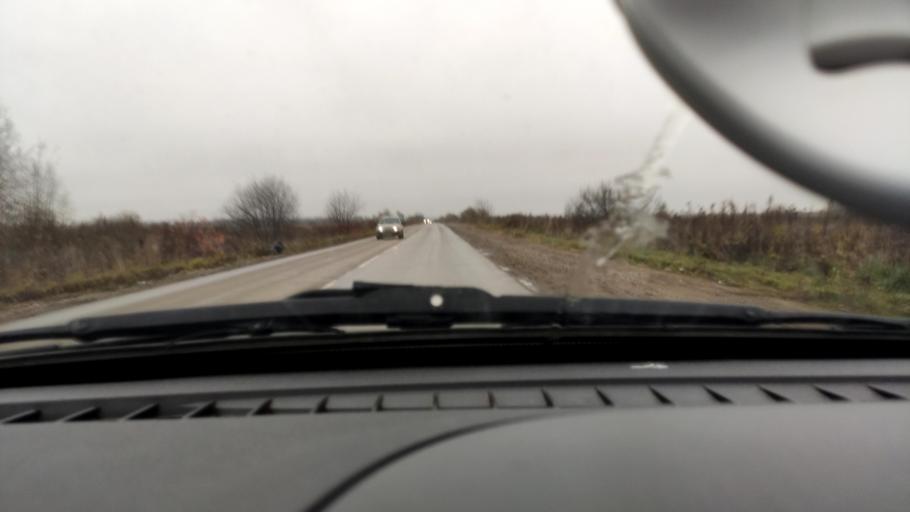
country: RU
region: Perm
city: Kondratovo
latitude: 58.0045
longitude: 56.0590
